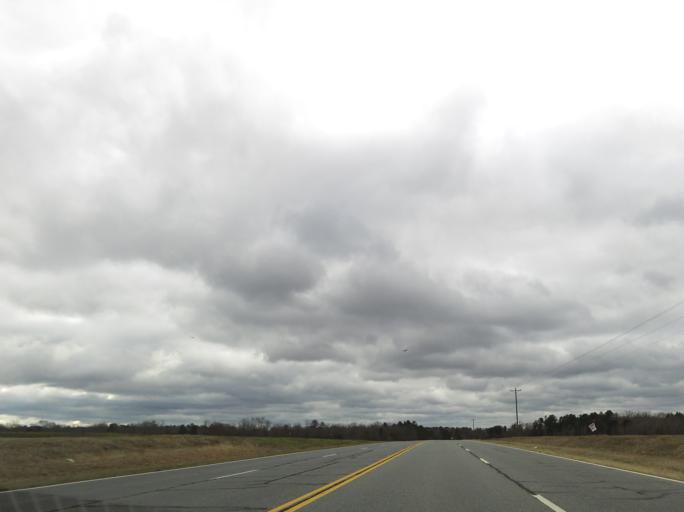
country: US
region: Georgia
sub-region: Bleckley County
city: Cochran
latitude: 32.4433
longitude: -83.3784
